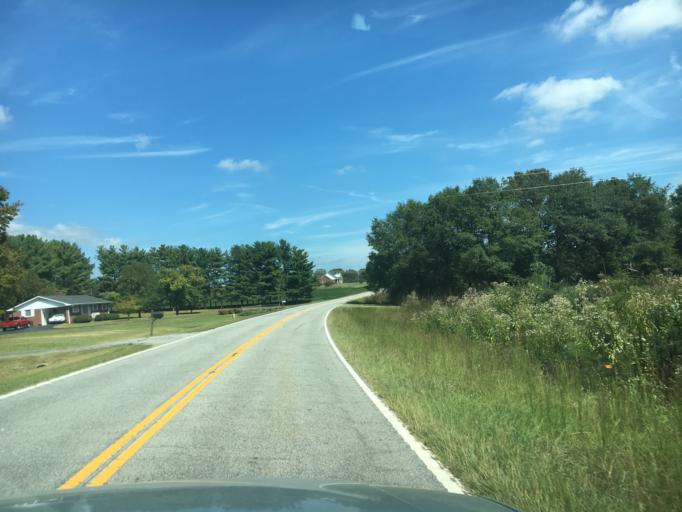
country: US
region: South Carolina
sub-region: Spartanburg County
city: Boiling Springs
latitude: 35.0907
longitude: -81.9297
